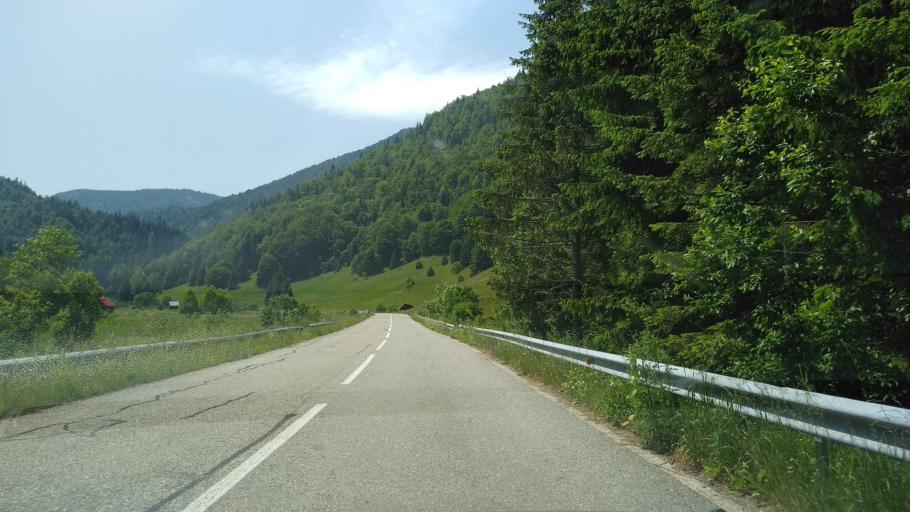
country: RO
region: Hunedoara
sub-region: Comuna Rau de Mori
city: Rau de Mori
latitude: 45.2789
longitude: 22.9286
